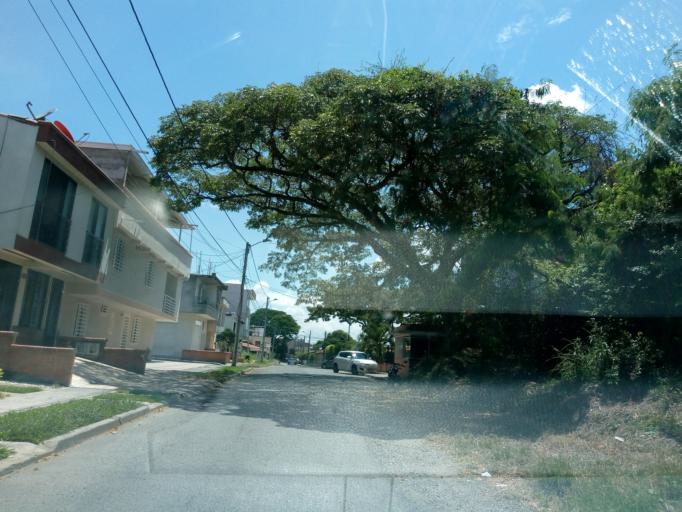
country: CO
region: Valle del Cauca
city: Cartago
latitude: 4.7474
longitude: -75.9251
